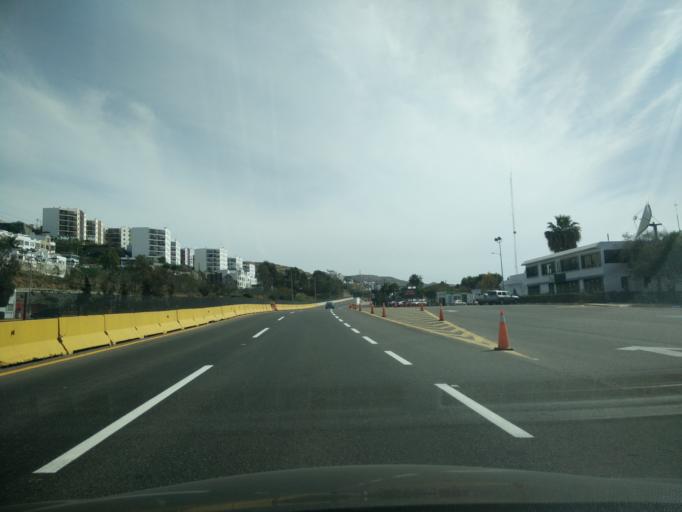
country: US
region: California
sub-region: San Diego County
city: Imperial Beach
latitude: 32.5272
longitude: -117.1080
